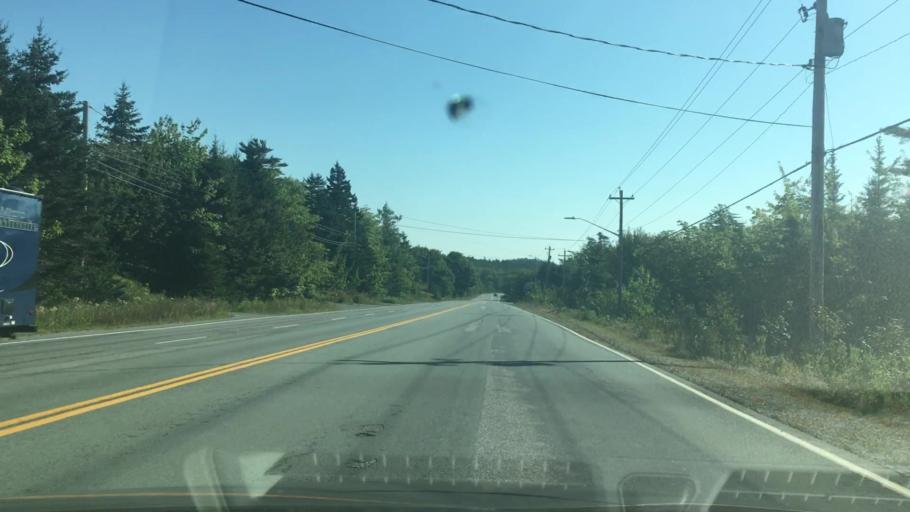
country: CA
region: Nova Scotia
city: Cole Harbour
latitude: 44.7783
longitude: -63.0871
